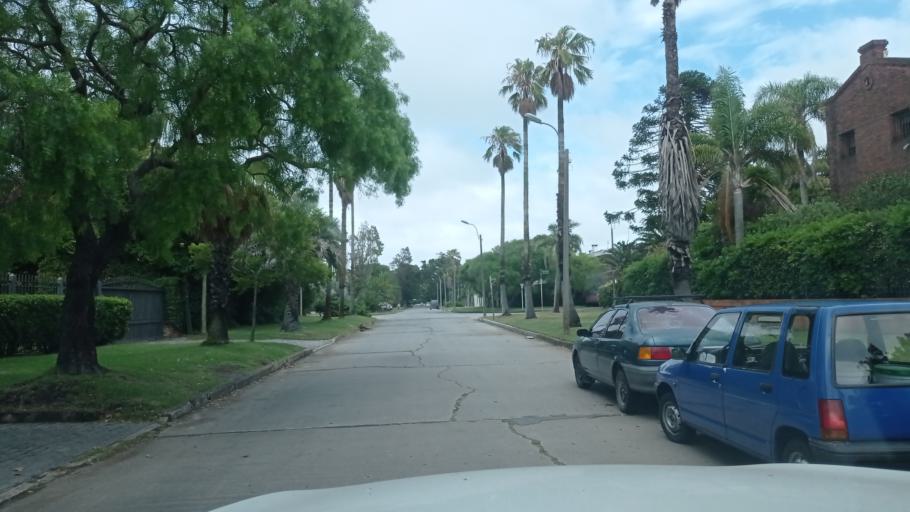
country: UY
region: Canelones
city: Barra de Carrasco
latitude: -34.8870
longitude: -56.0493
